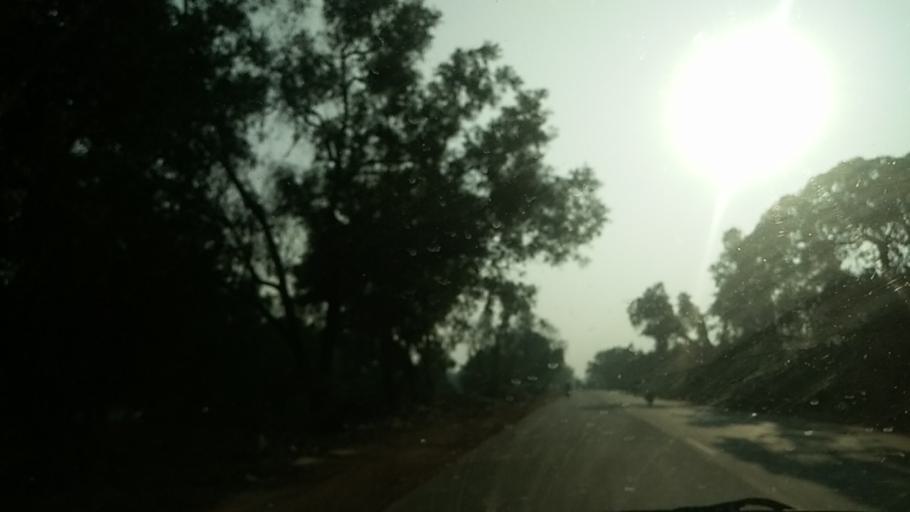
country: IN
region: Goa
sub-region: North Goa
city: Mapuca
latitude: 15.5849
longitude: 73.8175
